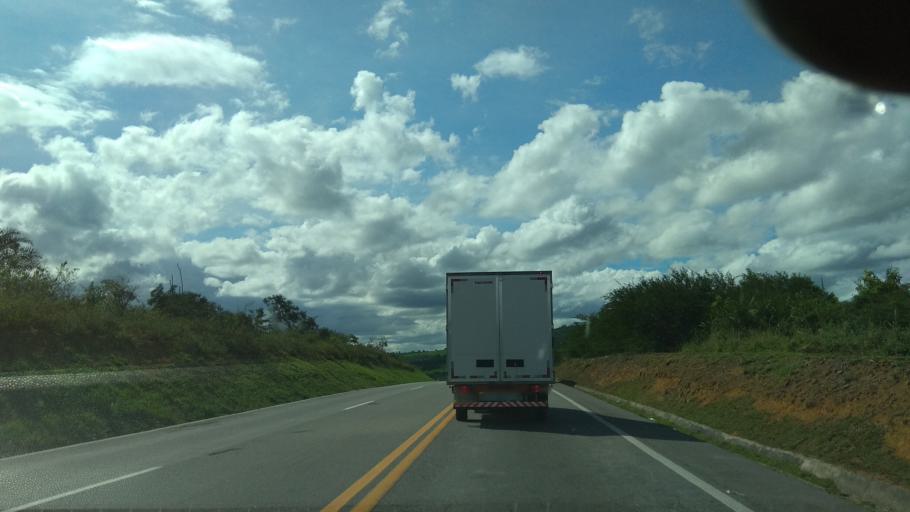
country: BR
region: Bahia
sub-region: Santa Ines
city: Santa Ines
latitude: -13.1702
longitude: -39.9980
